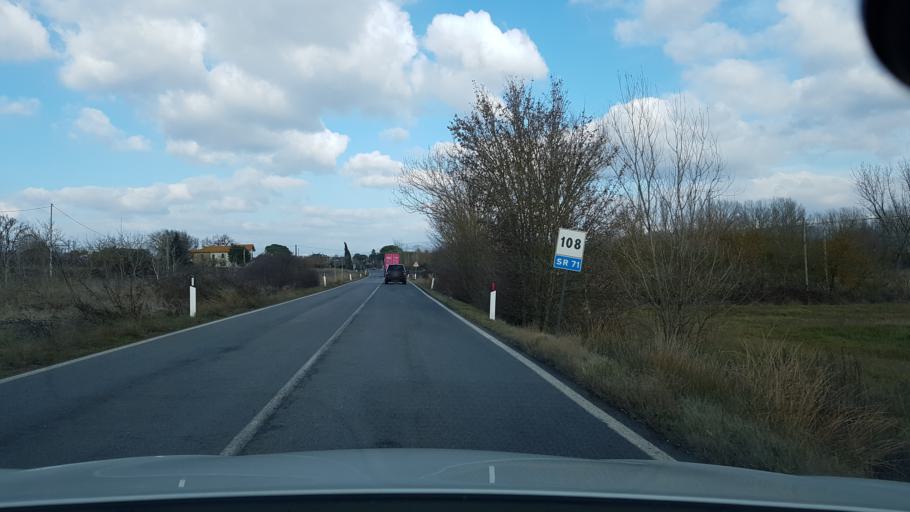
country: IT
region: Umbria
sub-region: Provincia di Perugia
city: Castiglione del Lago
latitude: 43.1629
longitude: 12.0157
